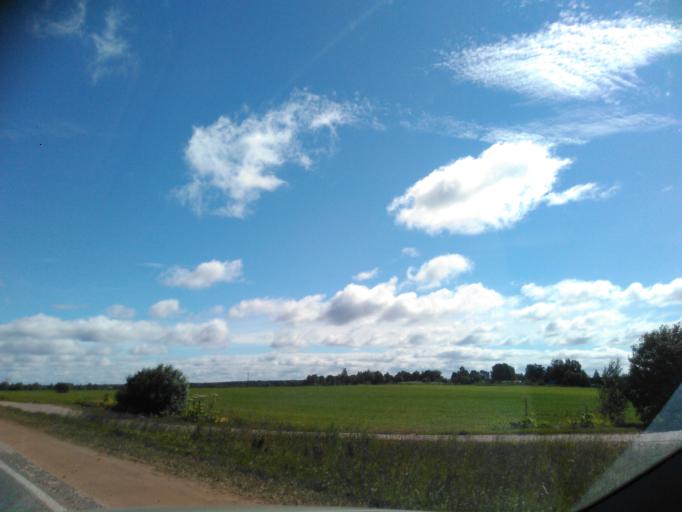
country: RU
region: Tverskaya
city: Zavidovo
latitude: 56.5928
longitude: 36.6119
